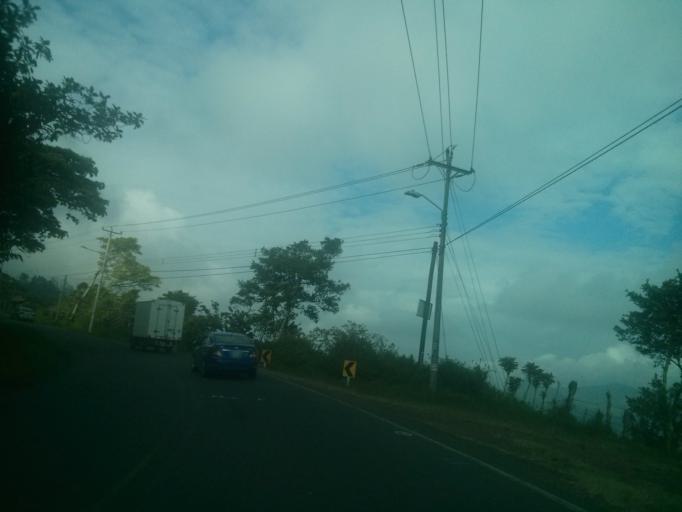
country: CR
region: Cartago
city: Paraiso
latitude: 9.8600
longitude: -83.8385
